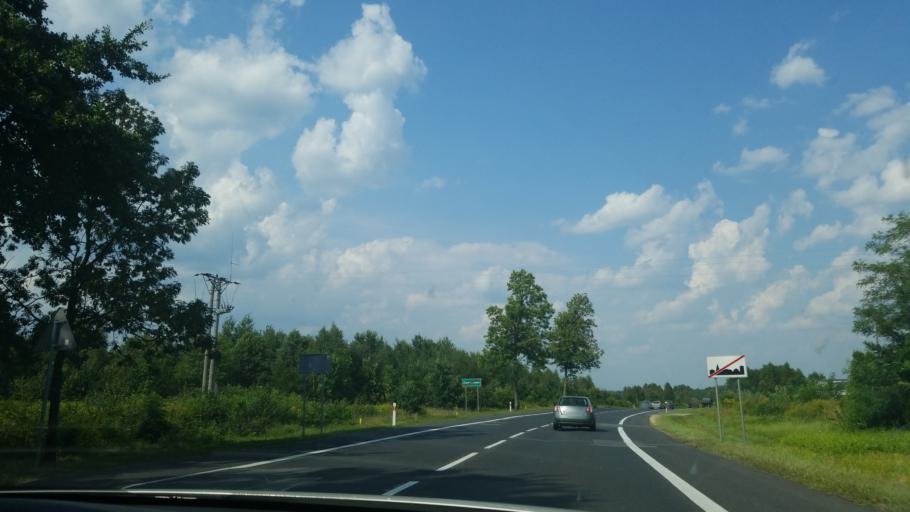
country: PL
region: Subcarpathian Voivodeship
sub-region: Powiat nizanski
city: Jarocin
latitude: 50.6070
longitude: 22.2790
